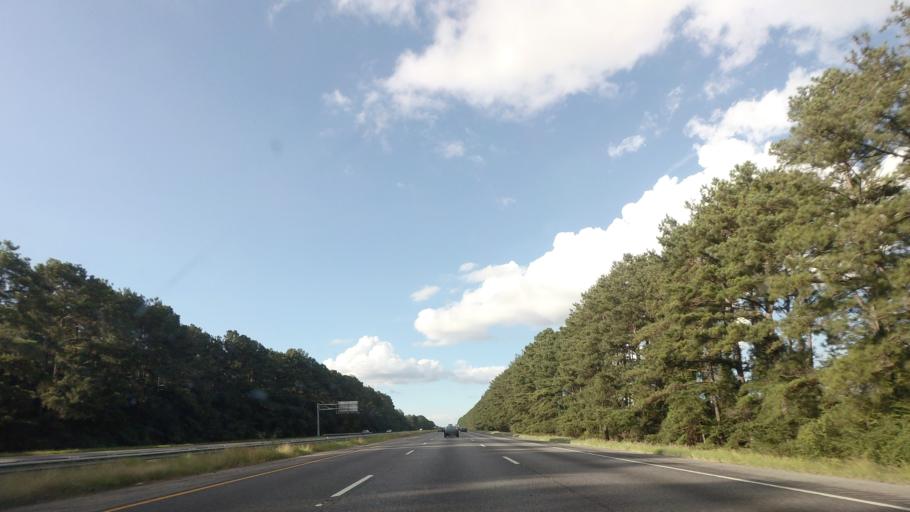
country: US
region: Georgia
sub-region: Houston County
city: Perry
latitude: 32.5027
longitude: -83.7428
